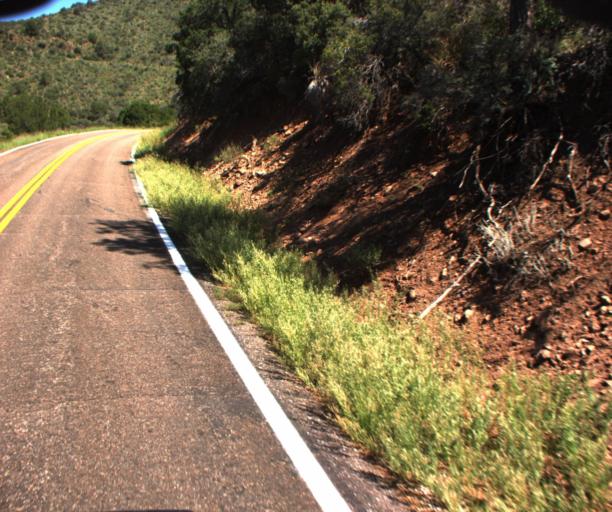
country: US
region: Arizona
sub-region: Greenlee County
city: Morenci
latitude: 33.2116
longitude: -109.3764
